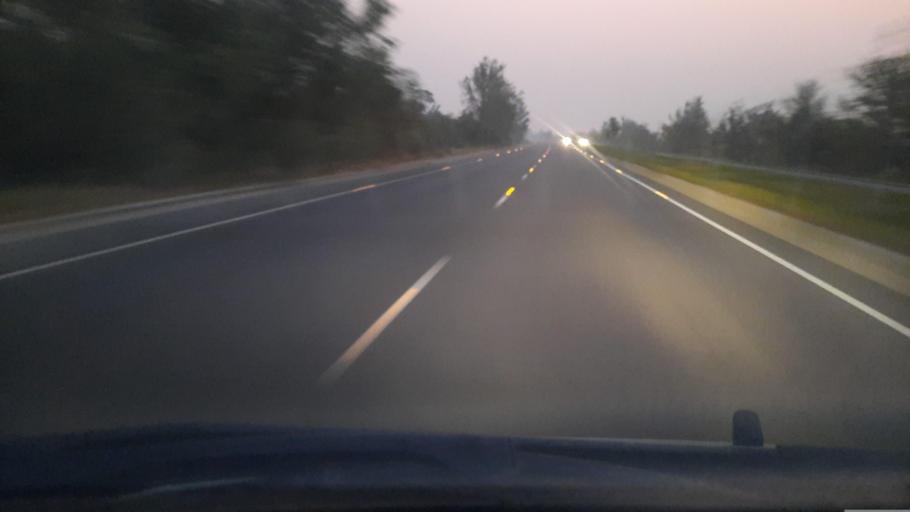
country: BD
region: Dhaka
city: Char Bhadrasan
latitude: 23.3980
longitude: 90.2263
